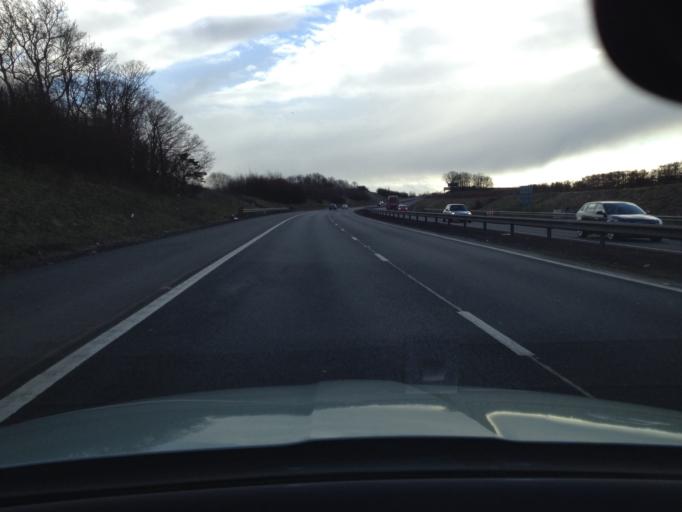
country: GB
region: Scotland
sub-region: Edinburgh
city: Kirkliston
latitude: 55.9690
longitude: -3.3888
